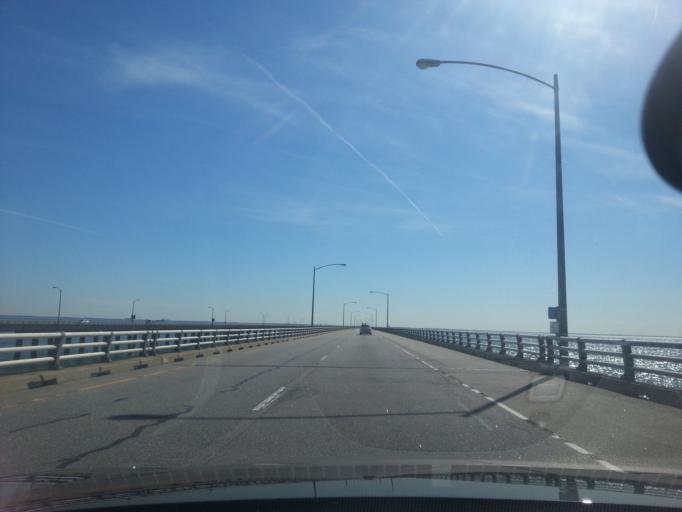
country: US
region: Virginia
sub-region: City of Virginia Beach
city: Virginia Beach
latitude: 37.0225
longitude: -76.0904
